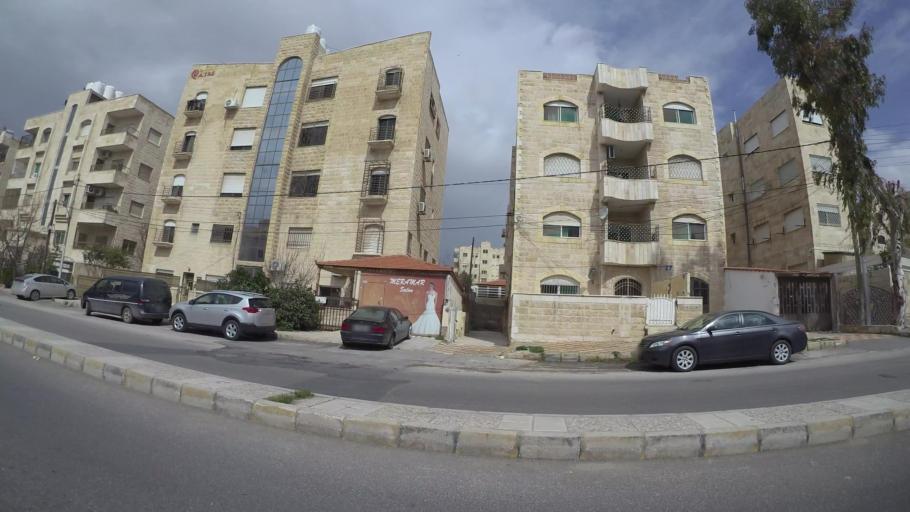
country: JO
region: Amman
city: Amman
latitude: 31.9879
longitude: 35.9220
